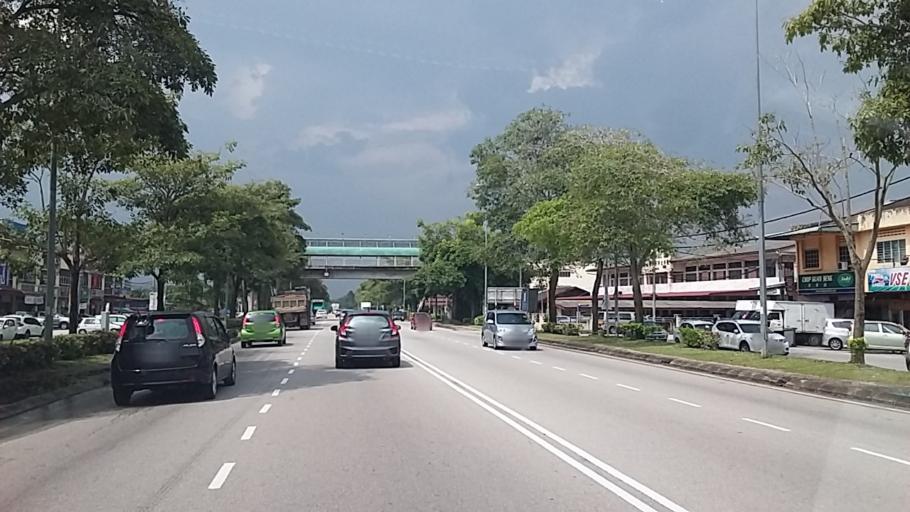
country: MY
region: Johor
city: Parit Raja
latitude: 1.8664
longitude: 103.1158
